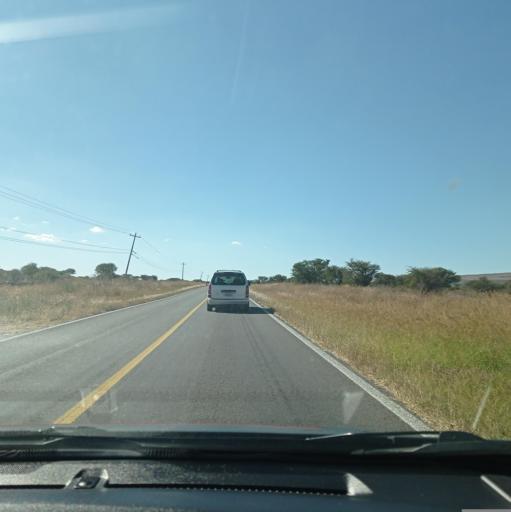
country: MX
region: Jalisco
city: San Miguel el Alto
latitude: 21.0204
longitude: -102.4528
